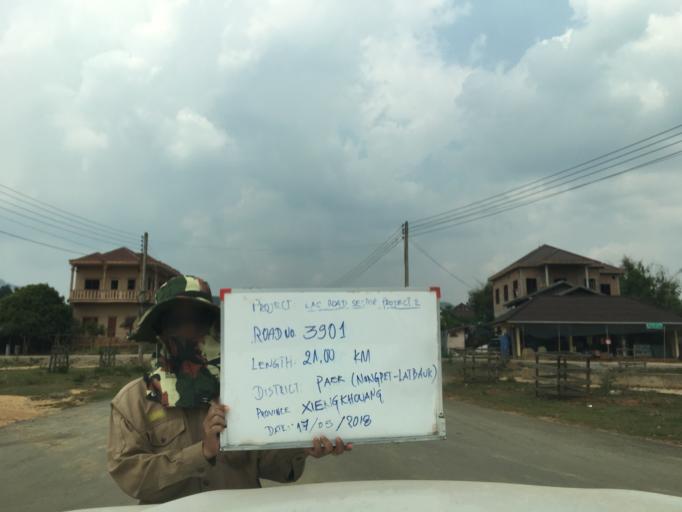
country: LA
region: Xiangkhoang
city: Muang Phonsavan
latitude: 19.5570
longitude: 103.3880
